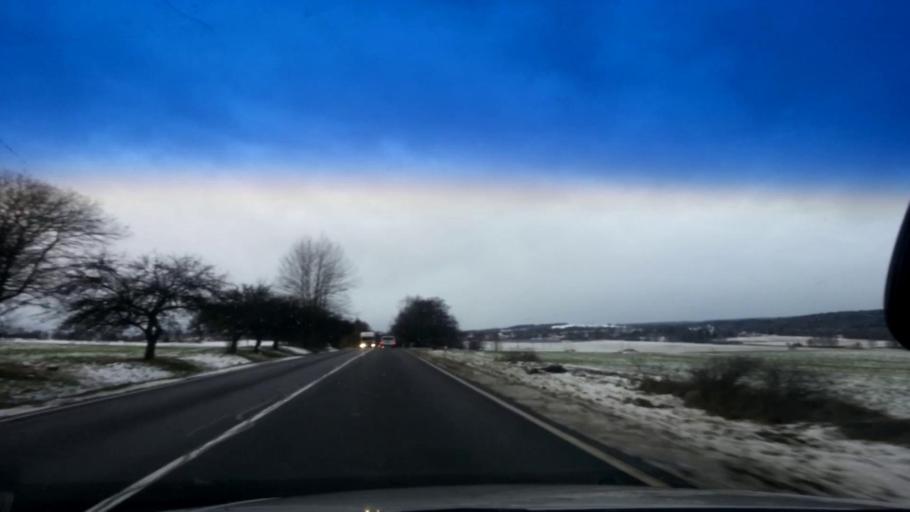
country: CZ
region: Karlovarsky
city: Hazlov
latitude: 50.1483
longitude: 12.2925
